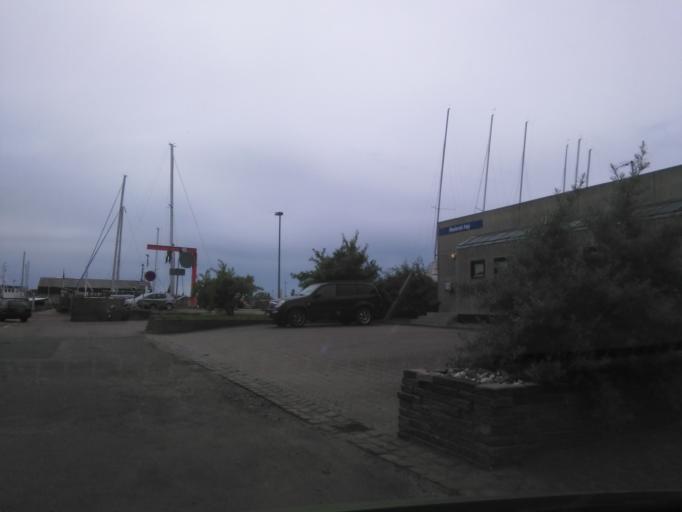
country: DK
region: Central Jutland
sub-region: Horsens Kommune
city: Horsens
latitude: 55.8575
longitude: 9.8719
